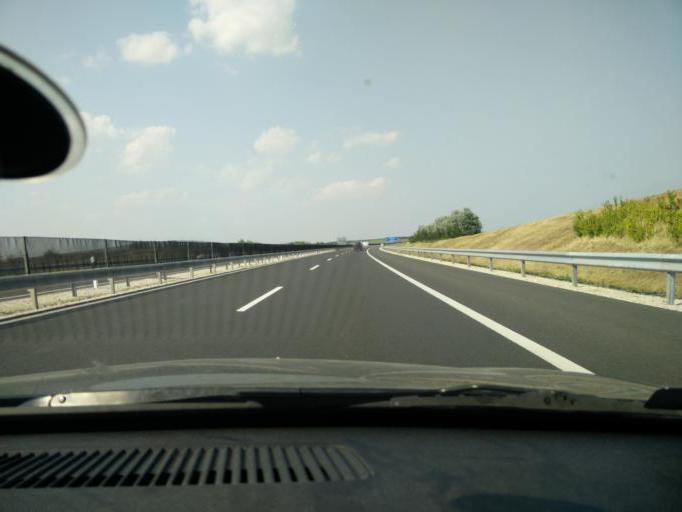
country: HU
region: Tolna
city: Szedres
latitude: 46.4610
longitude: 18.7088
